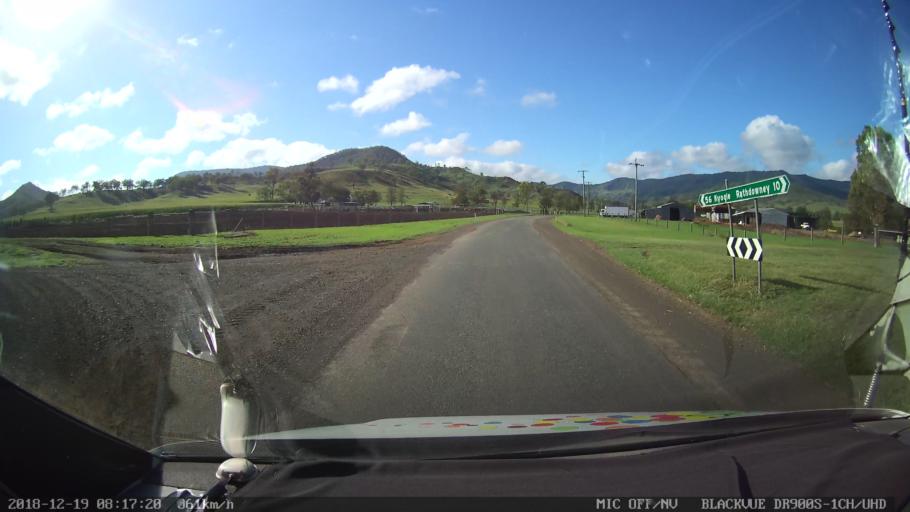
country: AU
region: New South Wales
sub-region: Kyogle
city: Kyogle
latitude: -28.2649
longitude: 152.9101
